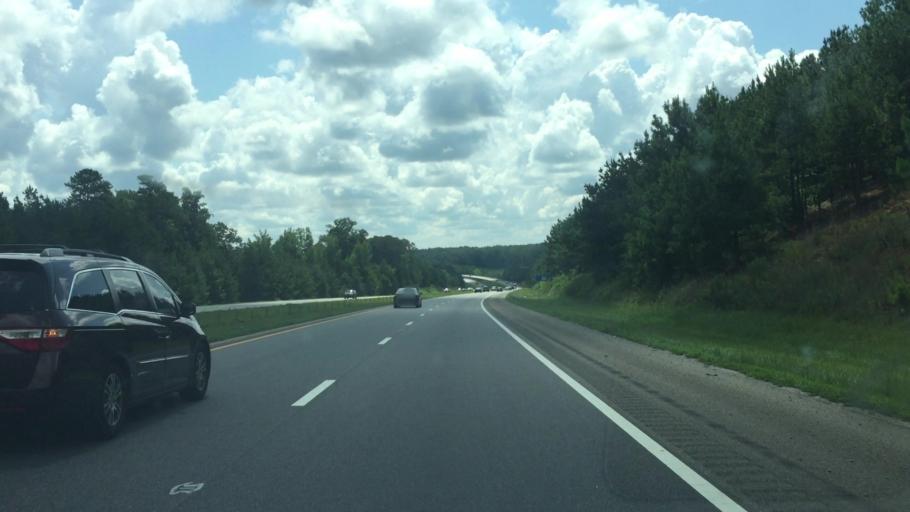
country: US
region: North Carolina
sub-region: Richmond County
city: Cordova
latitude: 34.9276
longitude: -79.8222
